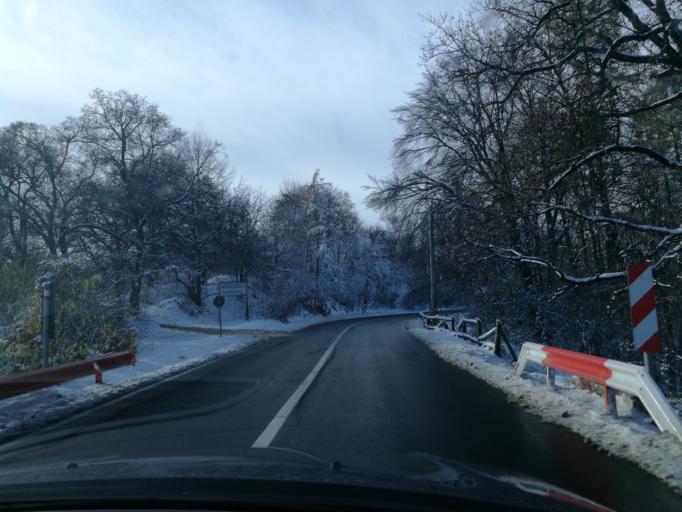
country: RO
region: Brasov
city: Brasov
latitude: 45.6455
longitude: 25.5749
